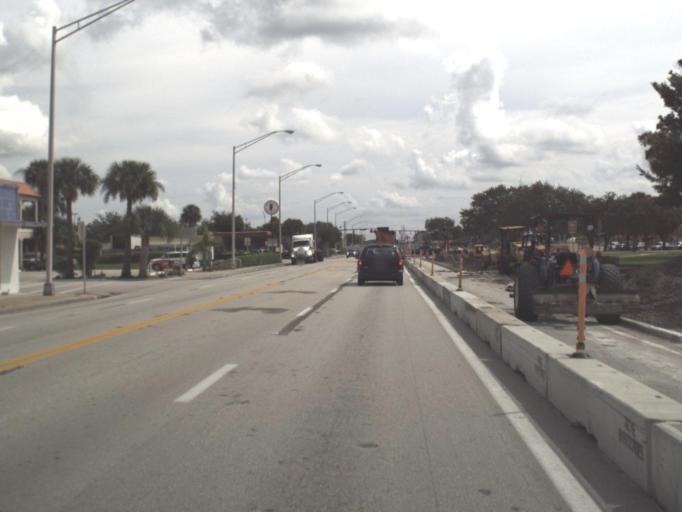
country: US
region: Florida
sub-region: Okeechobee County
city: Okeechobee
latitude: 27.2437
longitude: -80.8328
